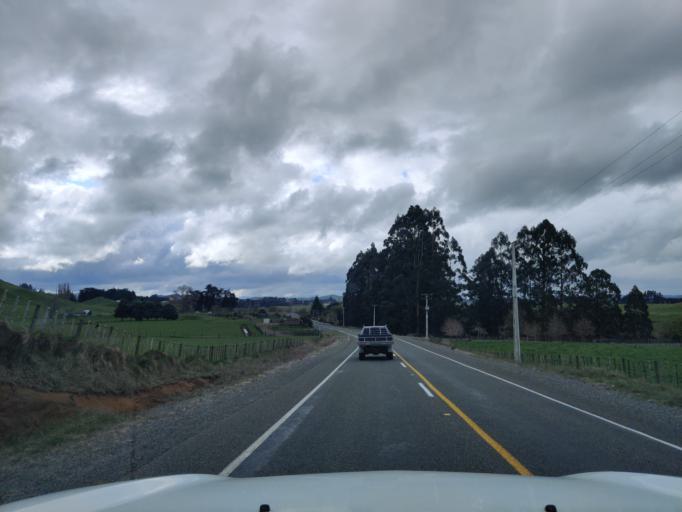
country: NZ
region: Manawatu-Wanganui
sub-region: Ruapehu District
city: Waiouru
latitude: -39.4510
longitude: 175.2925
